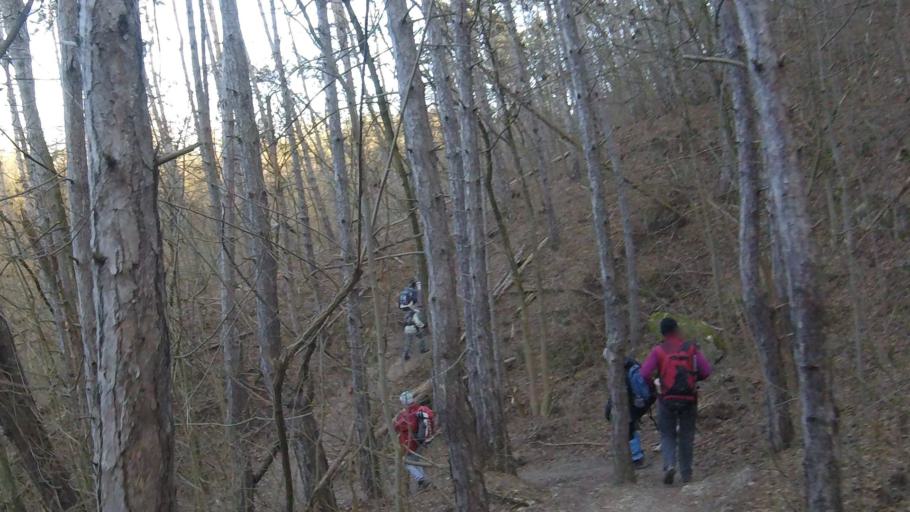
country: HU
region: Pest
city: Csobanka
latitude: 47.6141
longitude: 18.9584
